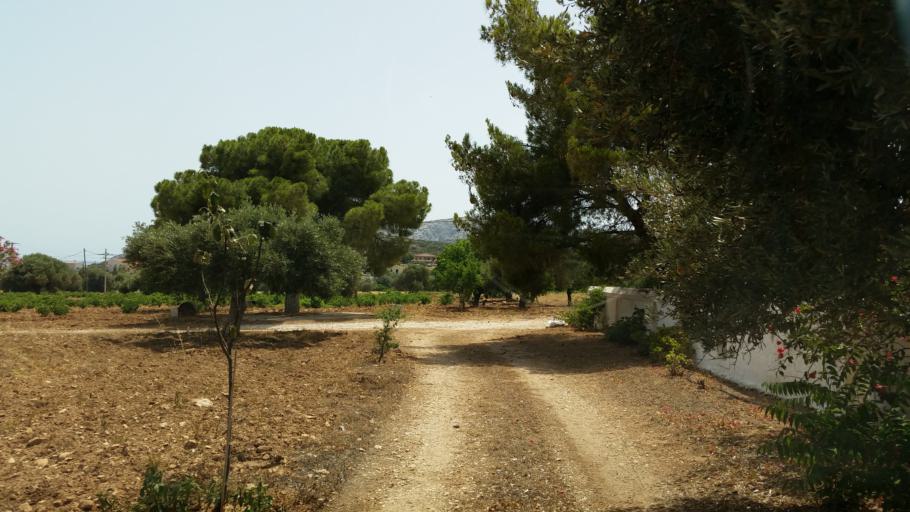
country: GR
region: Attica
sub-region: Nomarchia Anatolikis Attikis
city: Palaia Fokaia
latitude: 37.6733
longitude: 23.9668
